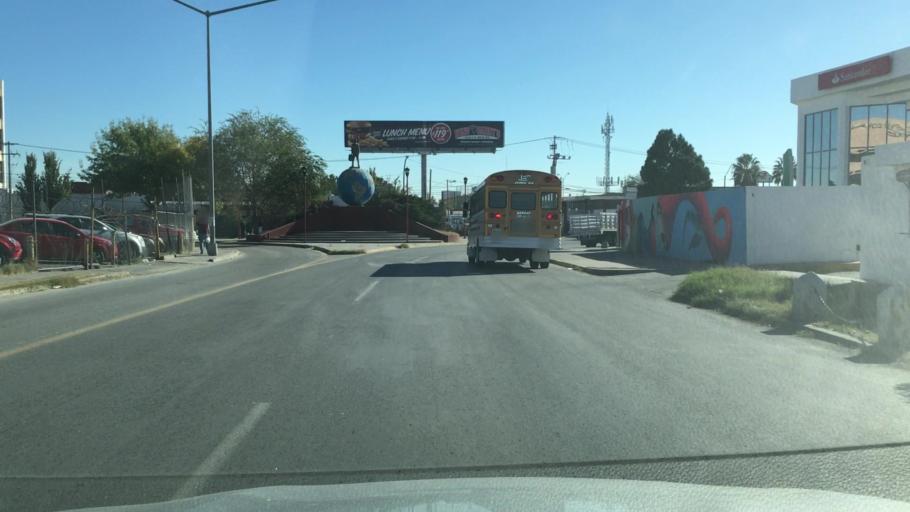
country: MX
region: Chihuahua
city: Ciudad Juarez
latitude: 31.7387
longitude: -106.4502
